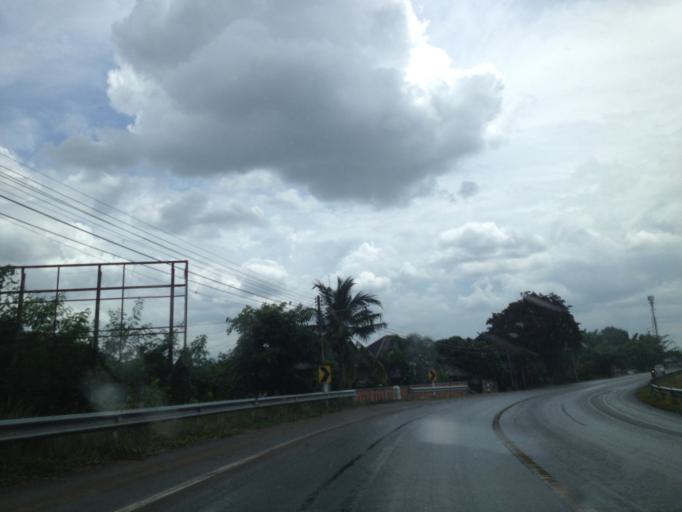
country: TH
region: Chiang Mai
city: San Pa Tong
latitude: 18.6388
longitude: 98.8482
